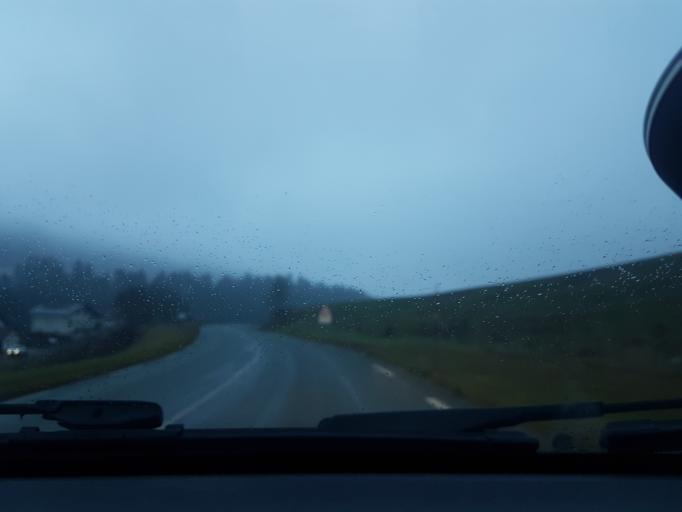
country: FR
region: Franche-Comte
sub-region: Departement du Doubs
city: La Cluse-et-Mijoux
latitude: 46.8954
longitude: 6.4453
